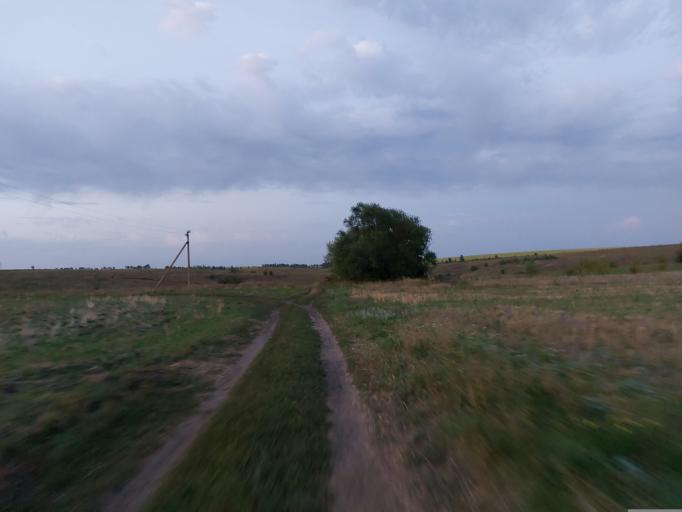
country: RU
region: Lipetsk
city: Dolgorukovo
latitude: 52.3837
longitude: 38.0499
